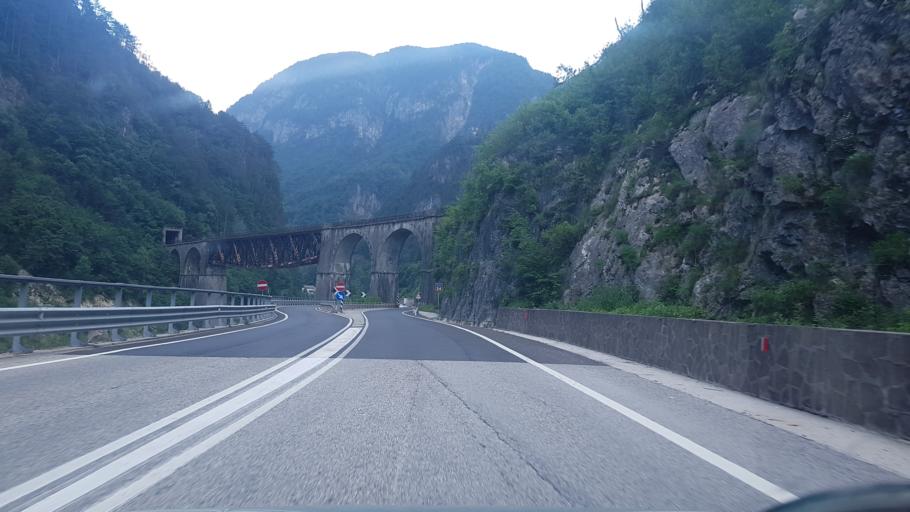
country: IT
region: Friuli Venezia Giulia
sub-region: Provincia di Udine
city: Dogna
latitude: 46.4677
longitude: 13.2938
